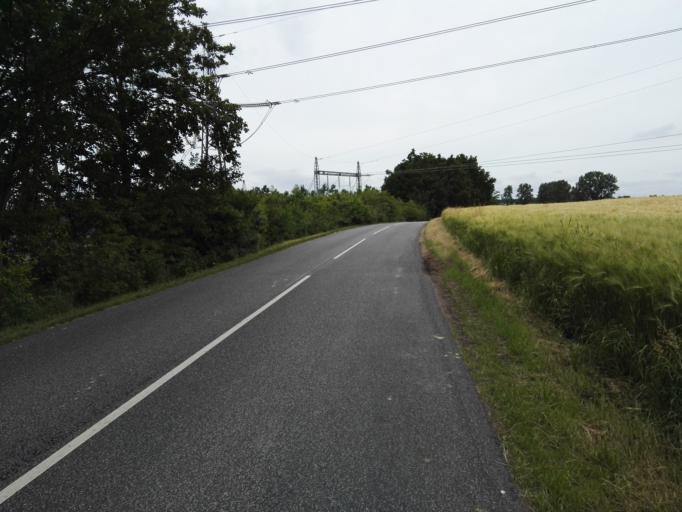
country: DK
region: Capital Region
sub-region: Egedal Kommune
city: Vekso
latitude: 55.7326
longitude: 12.2355
